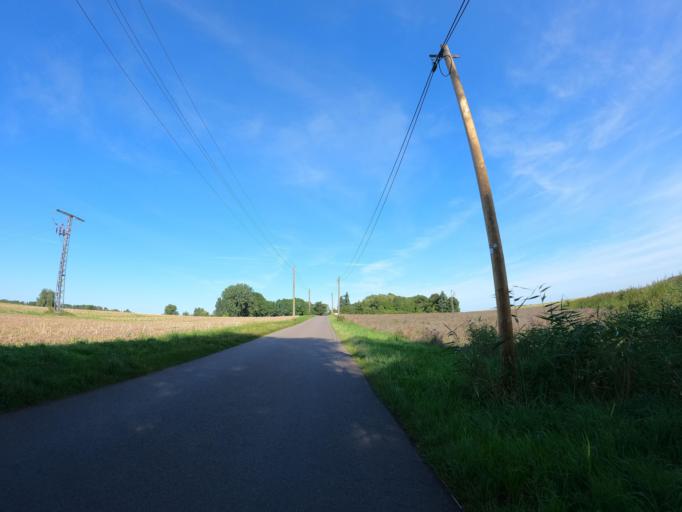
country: DE
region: Mecklenburg-Vorpommern
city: Kramerhof
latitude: 54.3709
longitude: 13.0489
